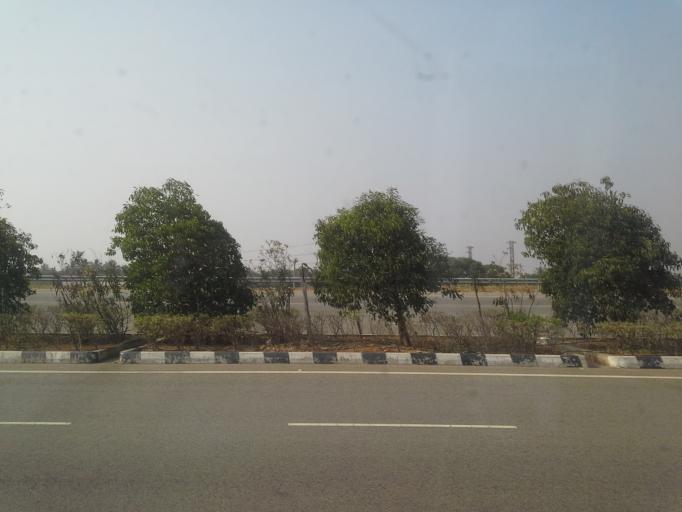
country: IN
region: Telangana
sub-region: Rangareddi
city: Sriramnagar
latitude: 17.2067
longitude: 78.3891
